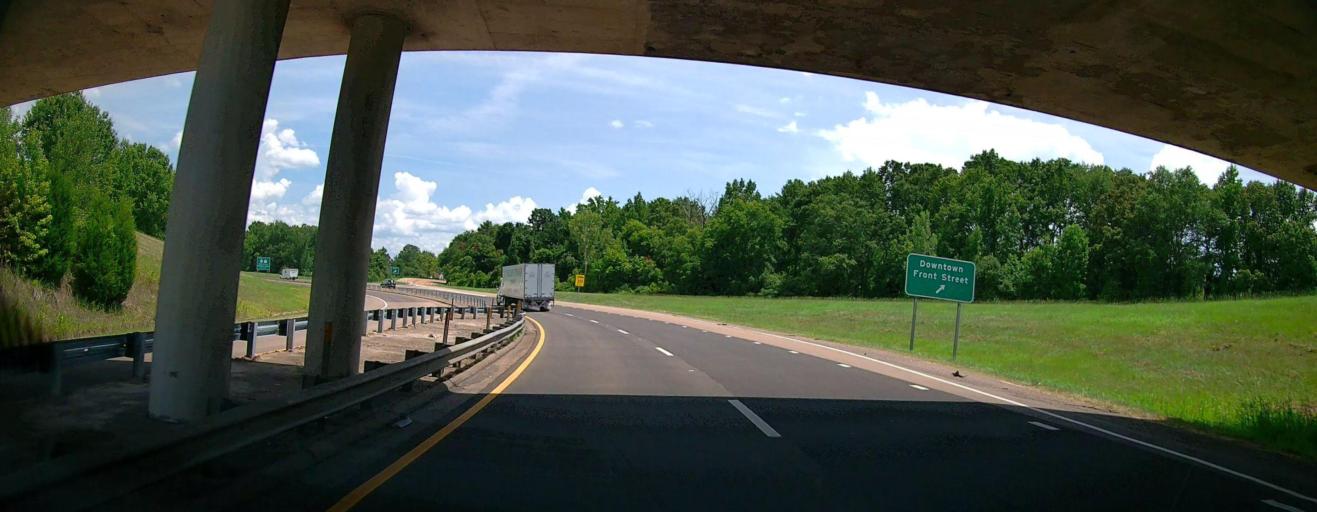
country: US
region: Mississippi
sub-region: Lee County
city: Tupelo
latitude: 34.2750
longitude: -88.7073
